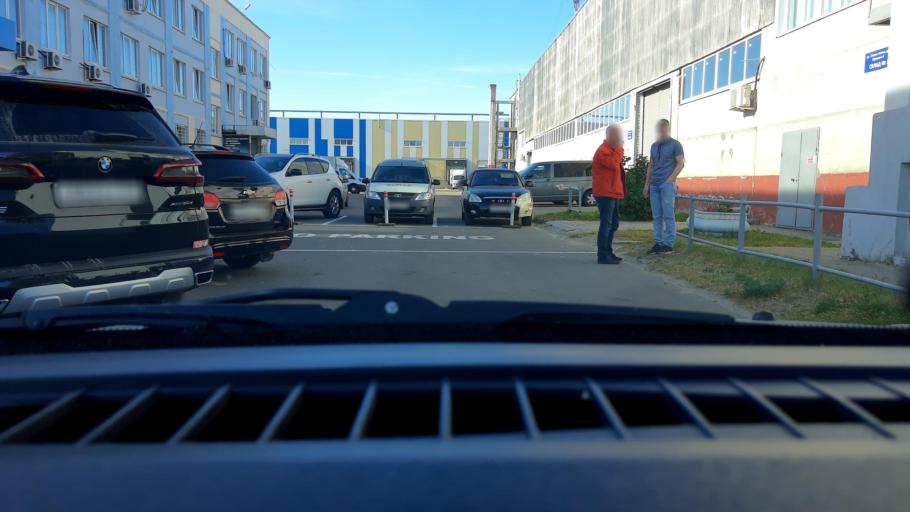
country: RU
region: Nizjnij Novgorod
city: Nizhniy Novgorod
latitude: 56.2483
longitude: 43.9362
